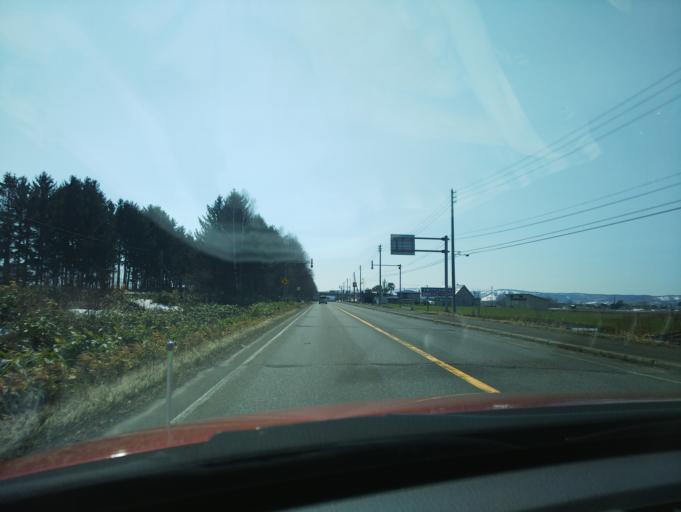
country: JP
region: Hokkaido
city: Nayoro
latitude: 44.3024
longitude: 142.4327
